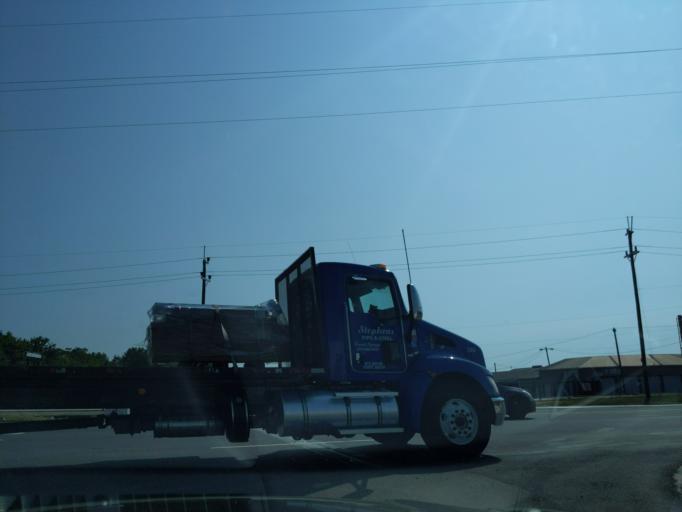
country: US
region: South Carolina
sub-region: Greenville County
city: Gantt
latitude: 34.8056
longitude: -82.4329
